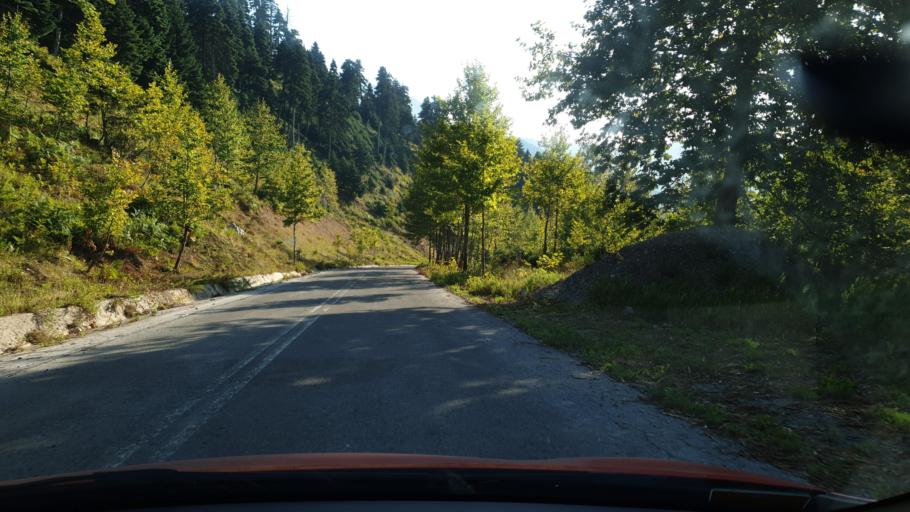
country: GR
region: Central Greece
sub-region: Nomos Evvoias
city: Yimnon
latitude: 38.6047
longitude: 23.9196
